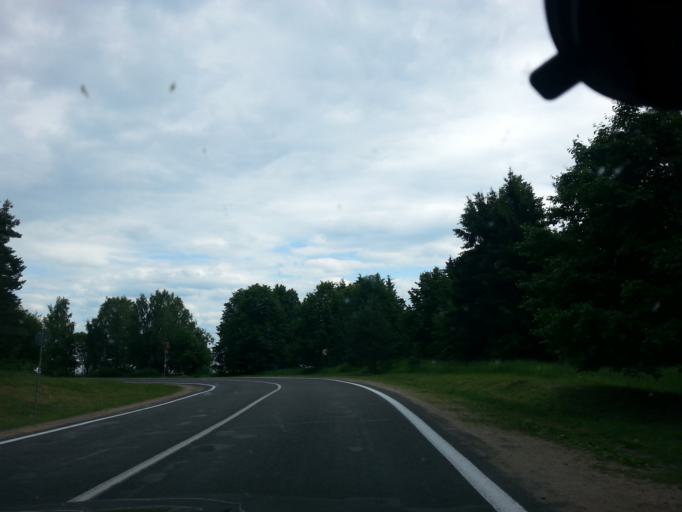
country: BY
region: Minsk
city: Narach
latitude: 54.9065
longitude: 26.7313
